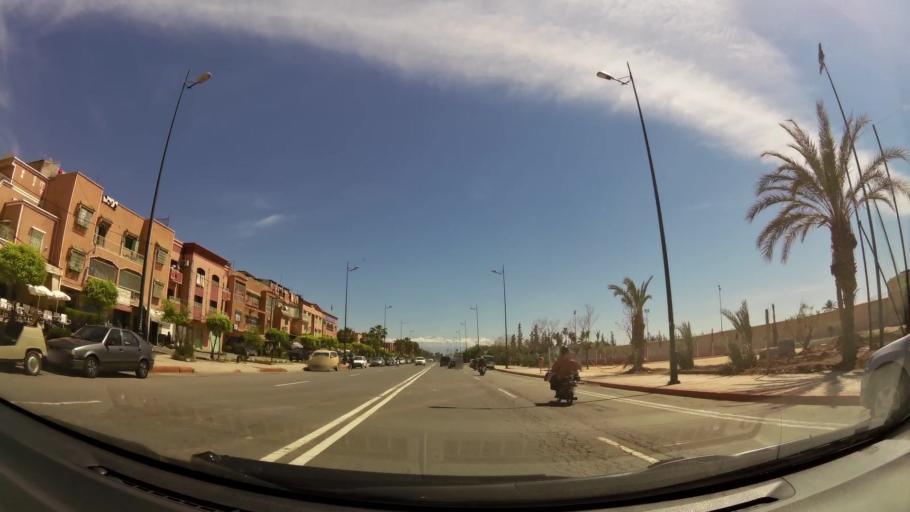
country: MA
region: Marrakech-Tensift-Al Haouz
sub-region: Marrakech
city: Marrakesh
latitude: 31.6063
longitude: -7.9729
